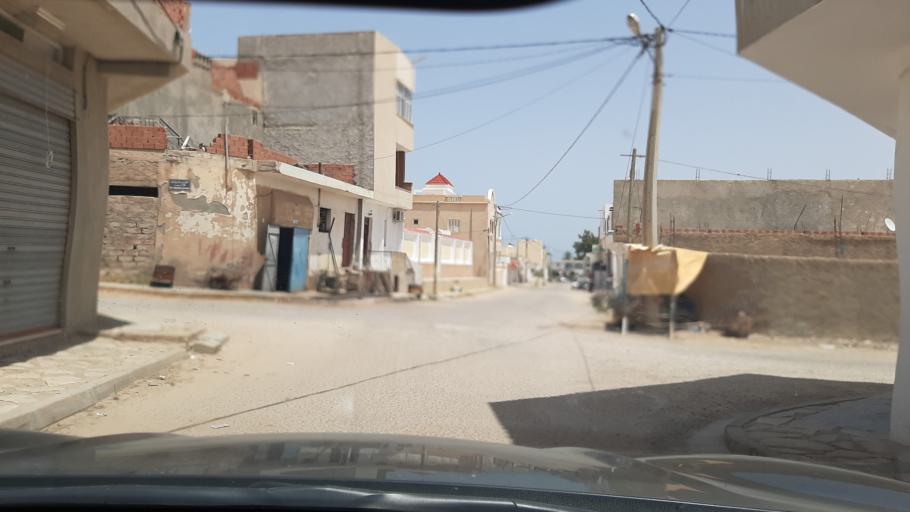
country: TN
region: Qabis
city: Matmata
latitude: 33.6176
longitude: 10.2826
